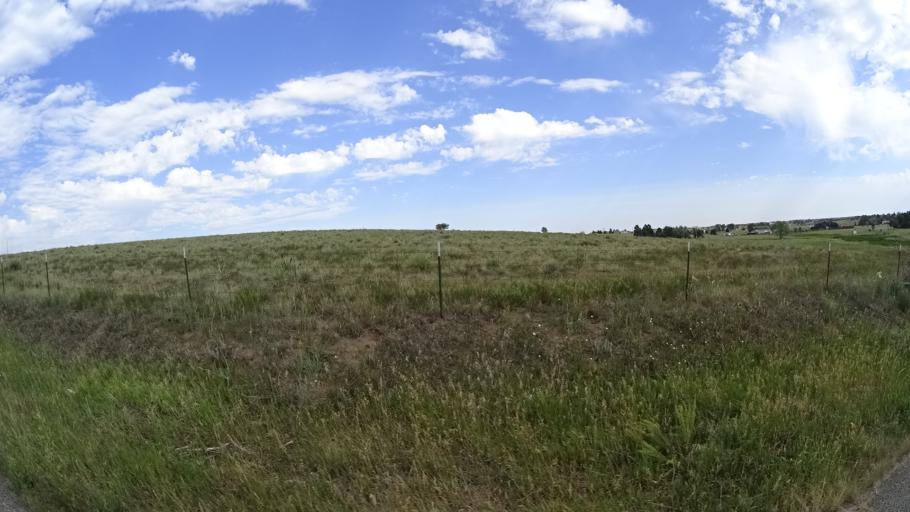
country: US
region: Colorado
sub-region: El Paso County
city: Cimarron Hills
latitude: 38.9093
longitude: -104.6767
